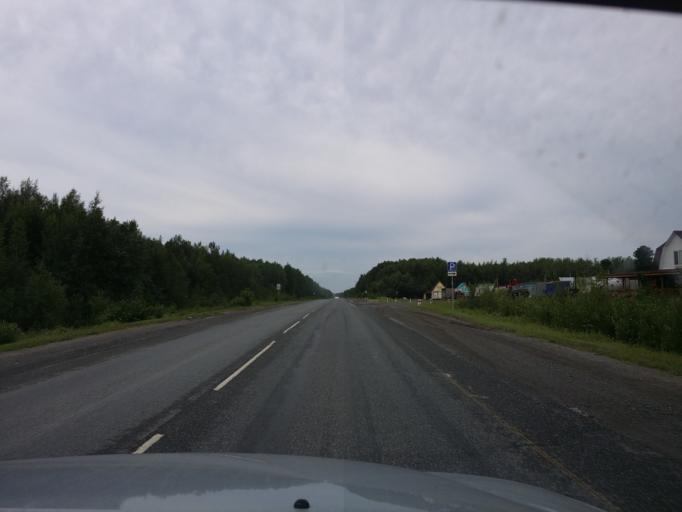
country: RU
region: Tjumen
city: Turtas
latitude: 58.9233
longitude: 69.0829
